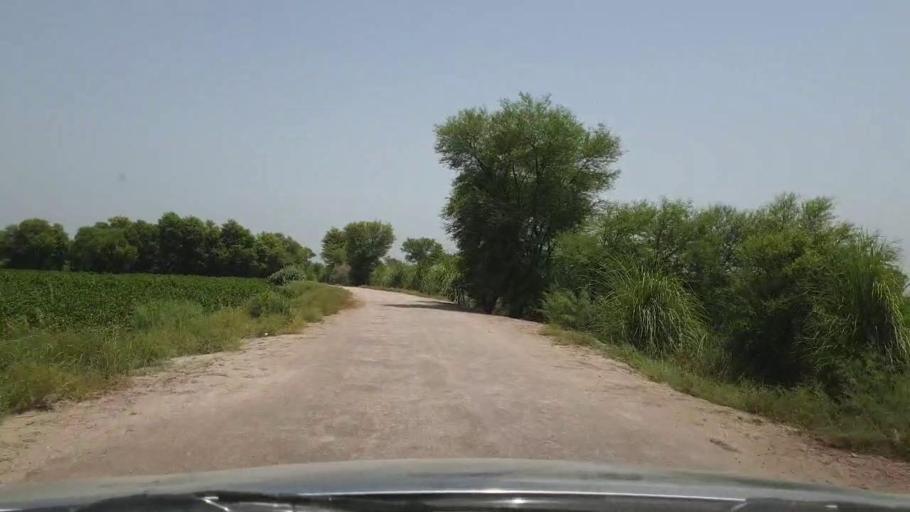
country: PK
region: Sindh
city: Pano Aqil
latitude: 27.8687
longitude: 69.1733
